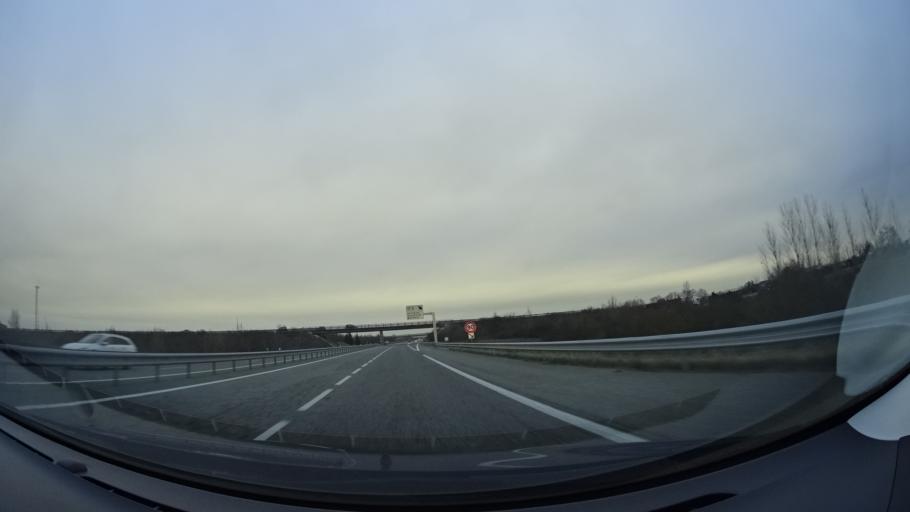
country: FR
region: Midi-Pyrenees
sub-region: Departement de l'Ariege
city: Mazeres
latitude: 43.2313
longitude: 1.6397
